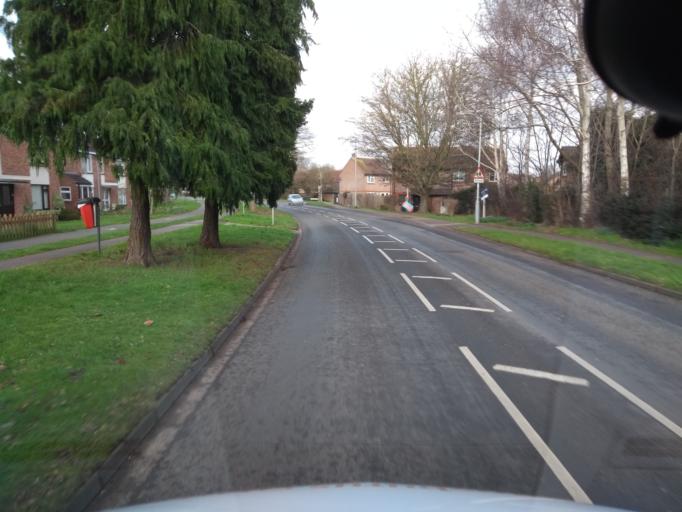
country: GB
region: England
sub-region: Somerset
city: Taunton
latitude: 51.0118
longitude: -3.0760
